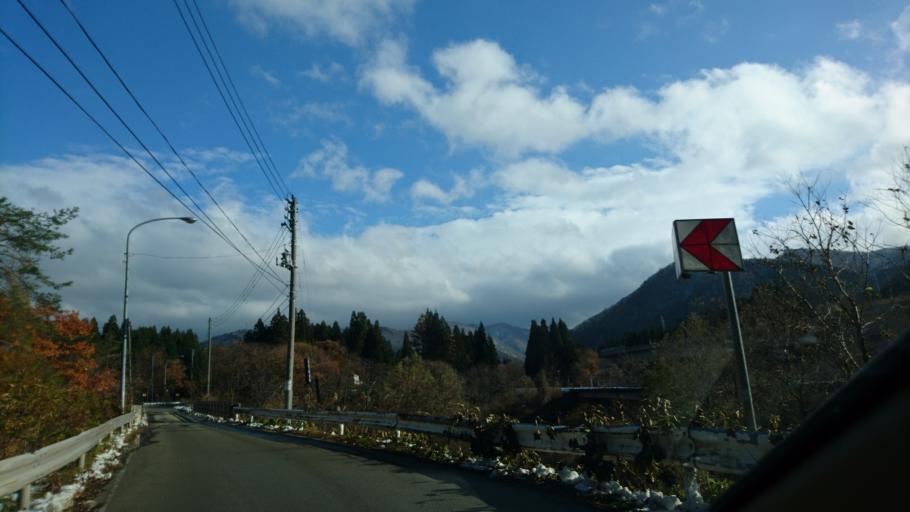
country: JP
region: Akita
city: Yokotemachi
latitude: 39.2985
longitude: 140.8296
